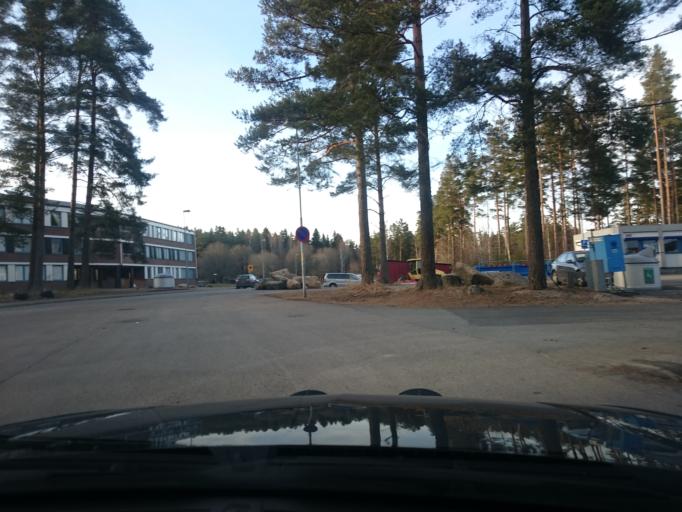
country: SE
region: Joenkoeping
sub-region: Vetlanda Kommun
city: Vetlanda
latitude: 57.4170
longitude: 15.0973
